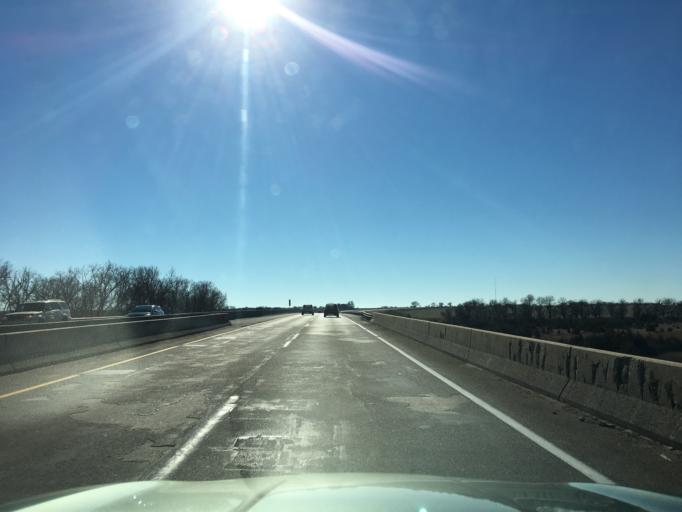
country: US
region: Kansas
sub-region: Sumner County
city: Belle Plaine
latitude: 37.3519
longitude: -97.3221
